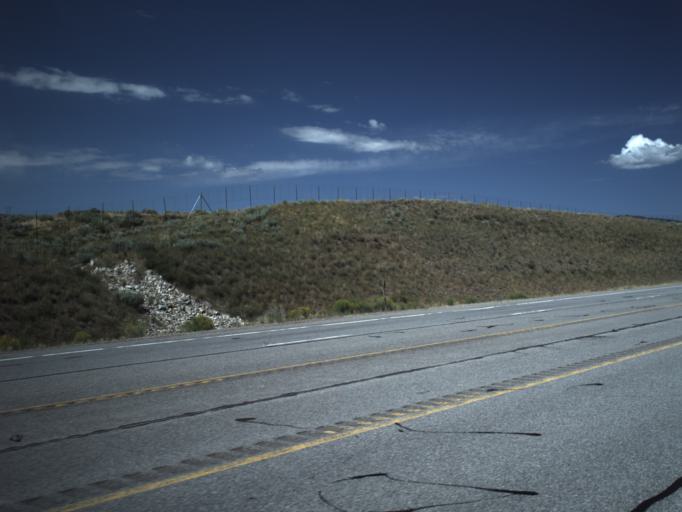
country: US
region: Utah
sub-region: Carbon County
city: Helper
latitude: 39.8365
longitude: -110.9781
